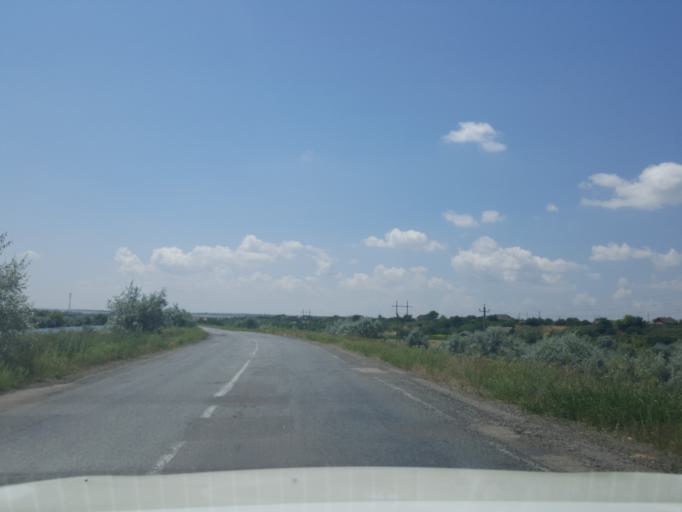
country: UA
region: Odessa
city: Bilyayivka
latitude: 46.4099
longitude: 30.1093
